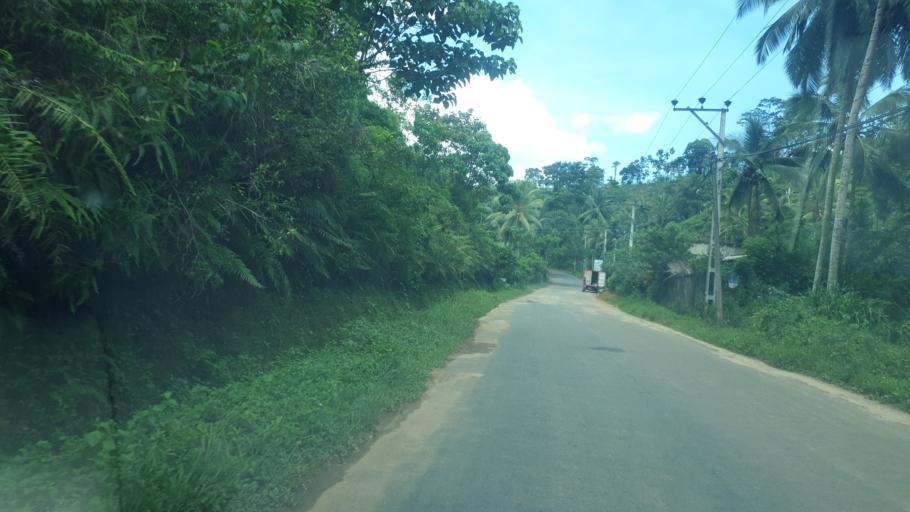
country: LK
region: Sabaragamuwa
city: Ratnapura
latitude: 6.4879
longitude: 80.4012
